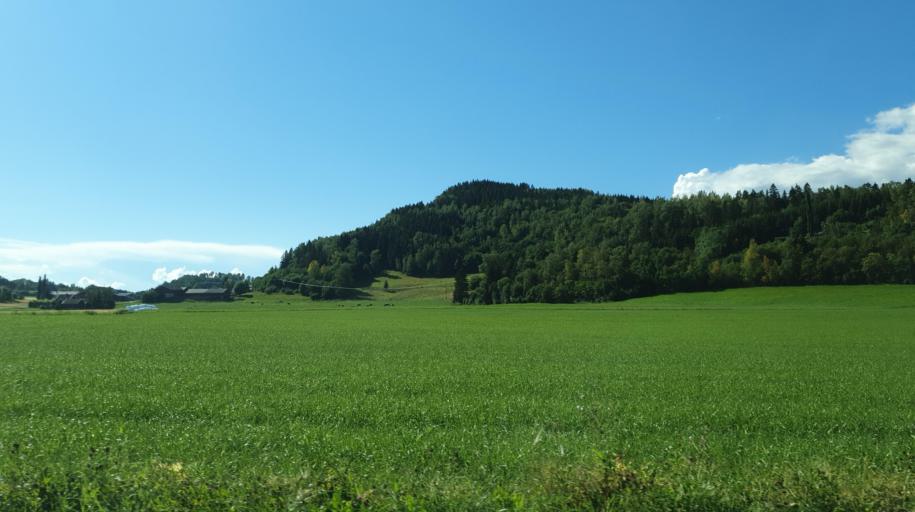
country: NO
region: Nord-Trondelag
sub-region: Verdal
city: Verdal
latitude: 63.7666
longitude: 11.4131
